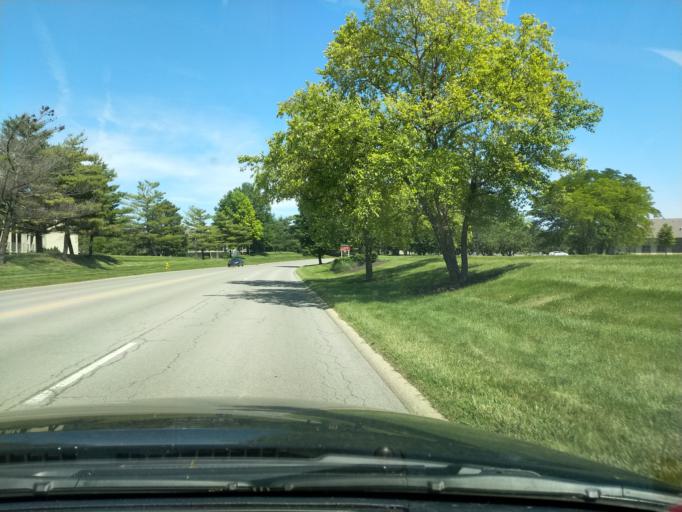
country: US
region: Indiana
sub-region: Hamilton County
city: Carmel
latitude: 39.9699
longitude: -86.1496
